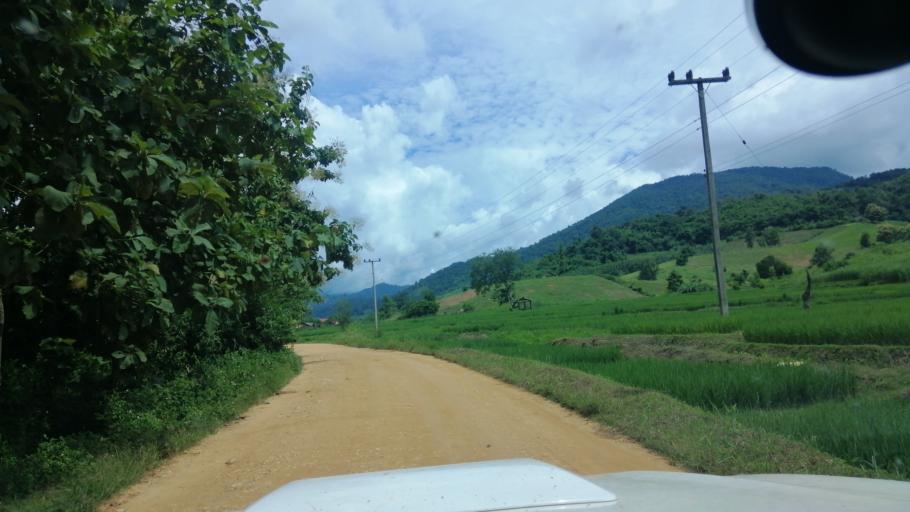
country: TH
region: Phayao
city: Phu Sang
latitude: 19.6811
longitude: 100.5030
